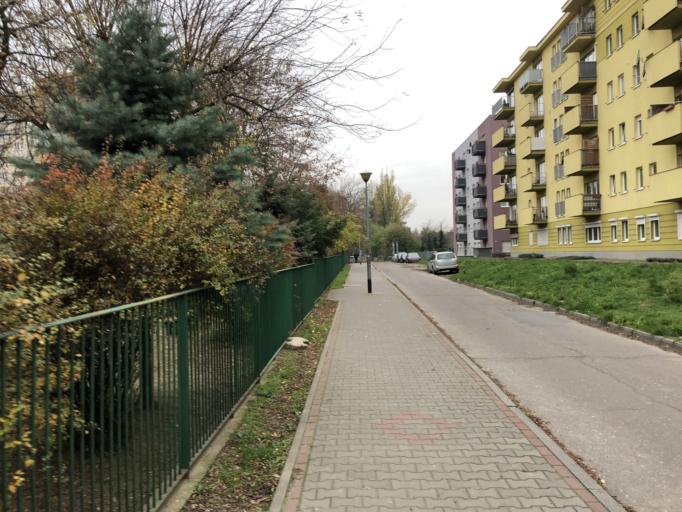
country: PL
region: Greater Poland Voivodeship
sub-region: Powiat poznanski
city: Lubon
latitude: 52.3898
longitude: 16.8625
